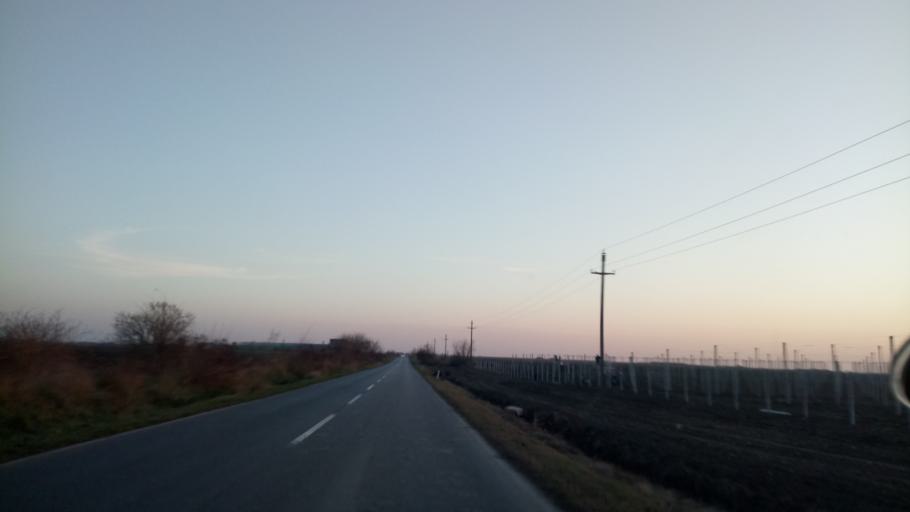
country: RS
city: Belegis
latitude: 45.0455
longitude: 20.3326
